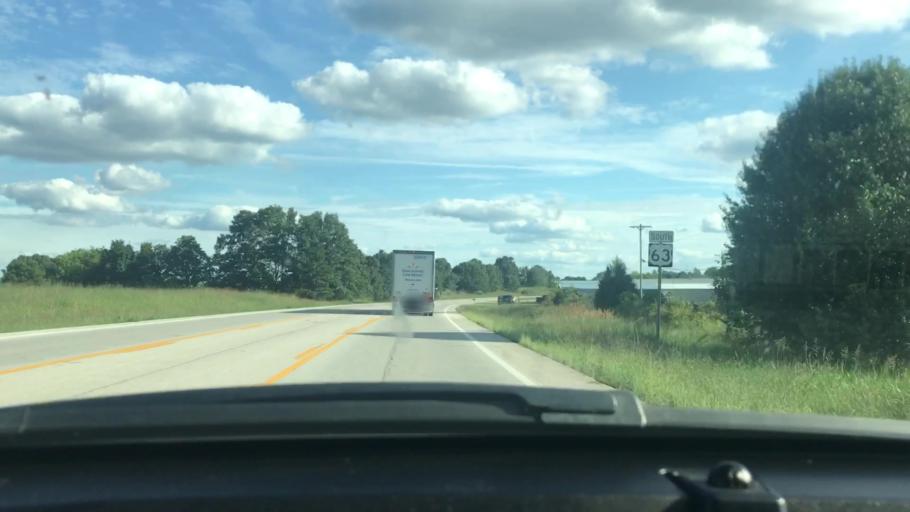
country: US
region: Missouri
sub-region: Oregon County
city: Thayer
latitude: 36.6056
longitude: -91.6447
